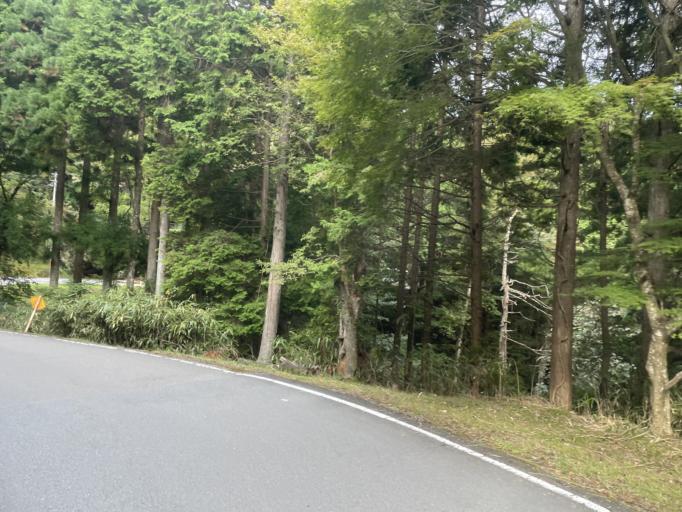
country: JP
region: Wakayama
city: Koya
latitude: 34.2227
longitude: 135.5761
